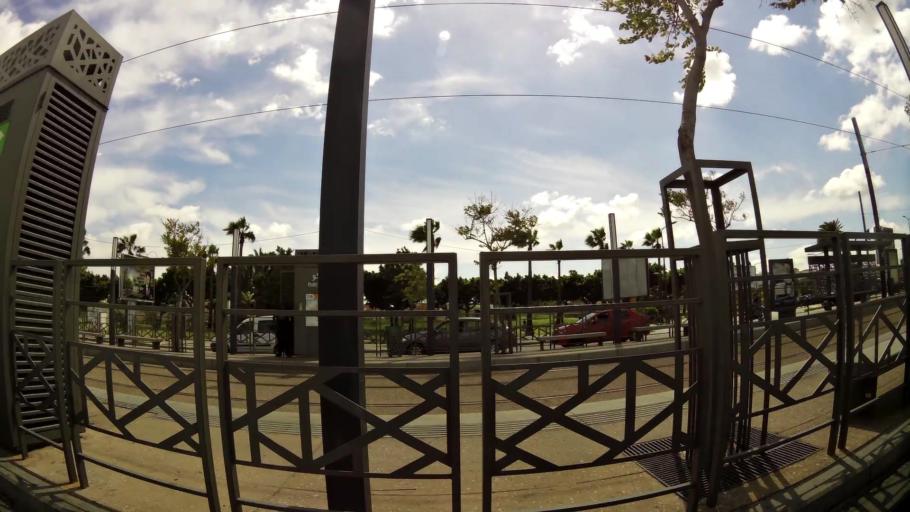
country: MA
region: Grand Casablanca
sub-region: Casablanca
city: Casablanca
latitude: 33.5640
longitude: -7.6275
